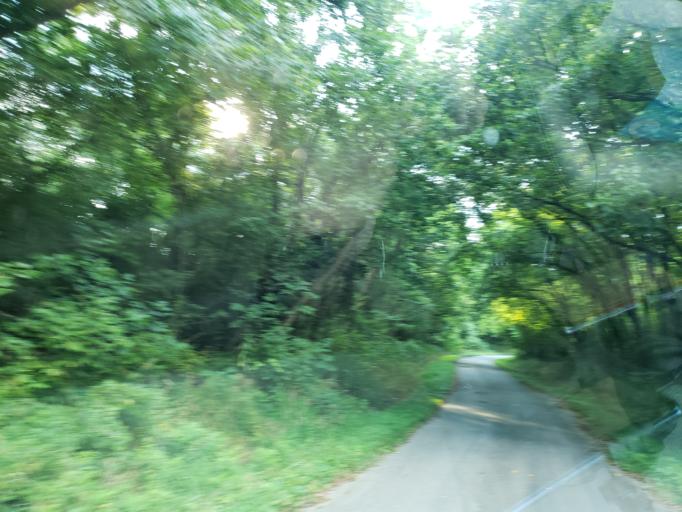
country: US
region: Georgia
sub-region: Polk County
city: Rockmart
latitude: 33.9857
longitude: -85.0433
